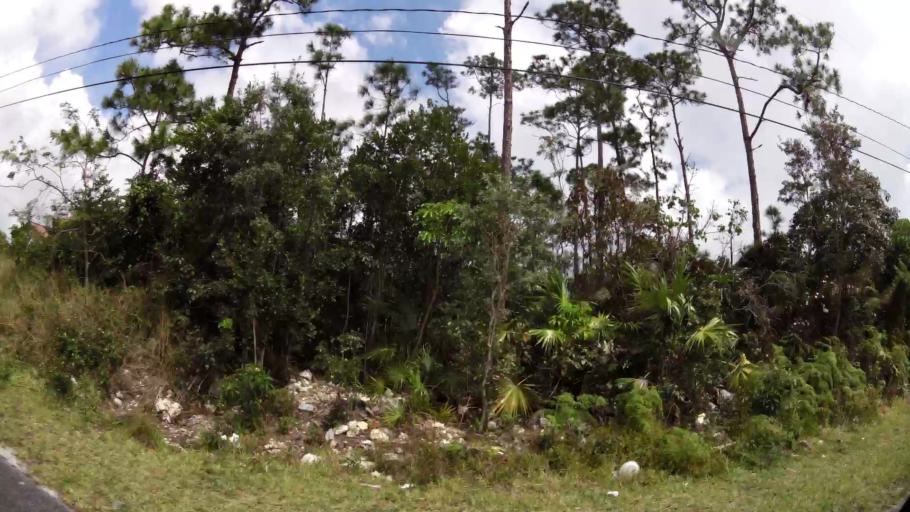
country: BS
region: Freeport
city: Lucaya
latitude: 26.5230
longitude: -78.6509
